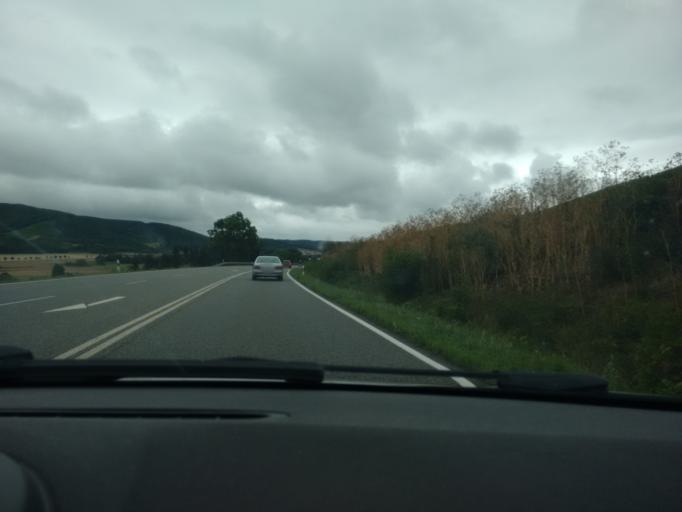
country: DE
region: Rheinland-Pfalz
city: Meddersheim
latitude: 49.7892
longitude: 7.6107
